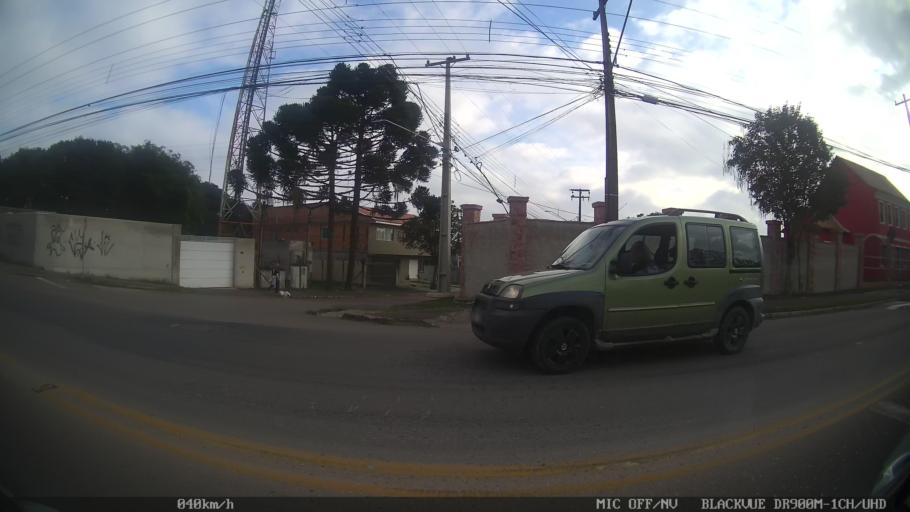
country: BR
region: Parana
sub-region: Almirante Tamandare
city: Almirante Tamandare
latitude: -25.3946
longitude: -49.3454
